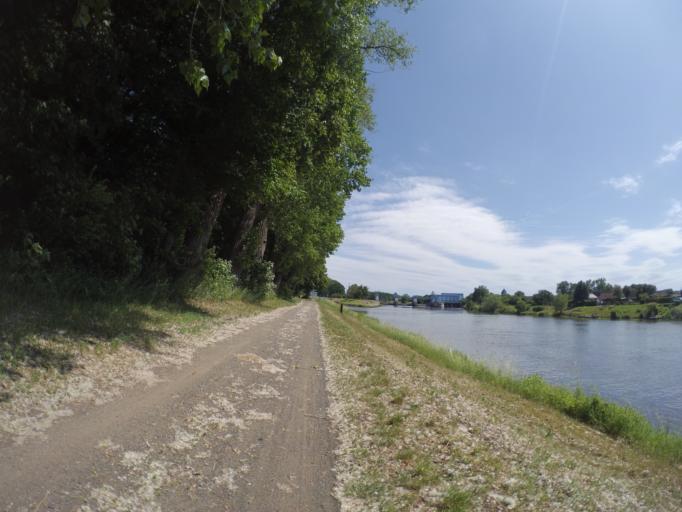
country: CZ
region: Central Bohemia
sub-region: Okres Nymburk
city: Sadska
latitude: 50.1719
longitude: 14.9363
